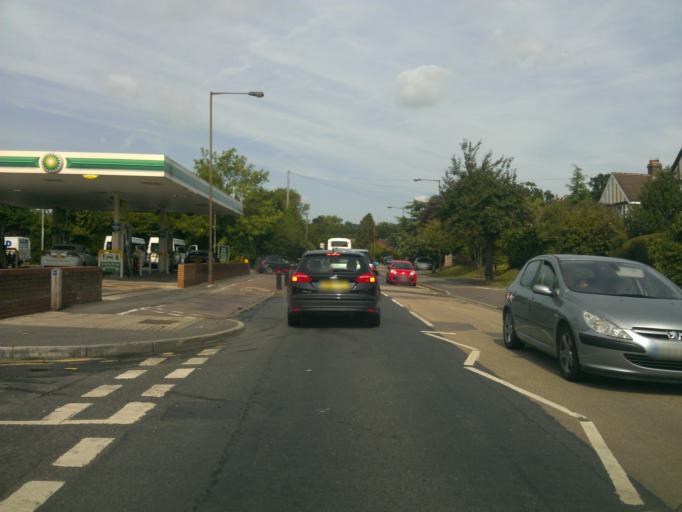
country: GB
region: England
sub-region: Kent
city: Tonbridge
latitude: 51.2091
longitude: 0.2576
